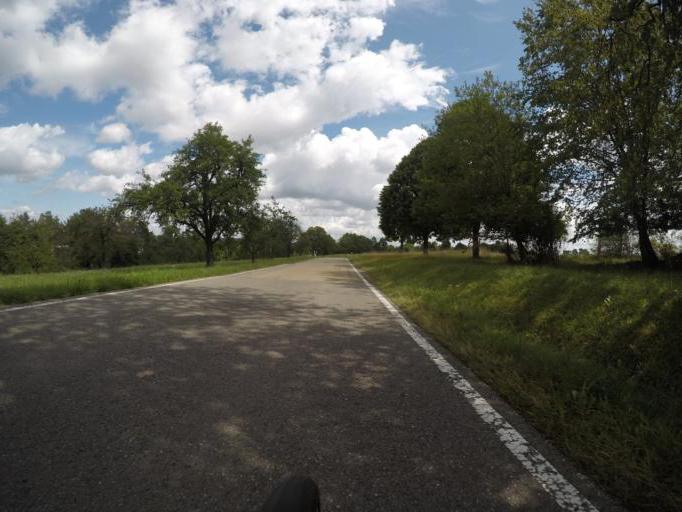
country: DE
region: Baden-Wuerttemberg
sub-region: Karlsruhe Region
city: Gechingen
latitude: 48.6710
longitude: 8.8524
